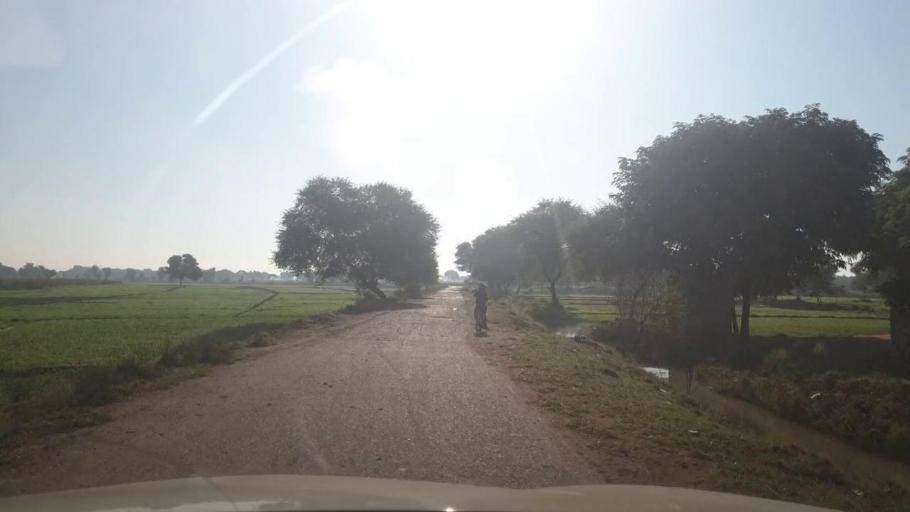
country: PK
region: Sindh
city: Bhan
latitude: 26.5427
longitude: 67.6838
